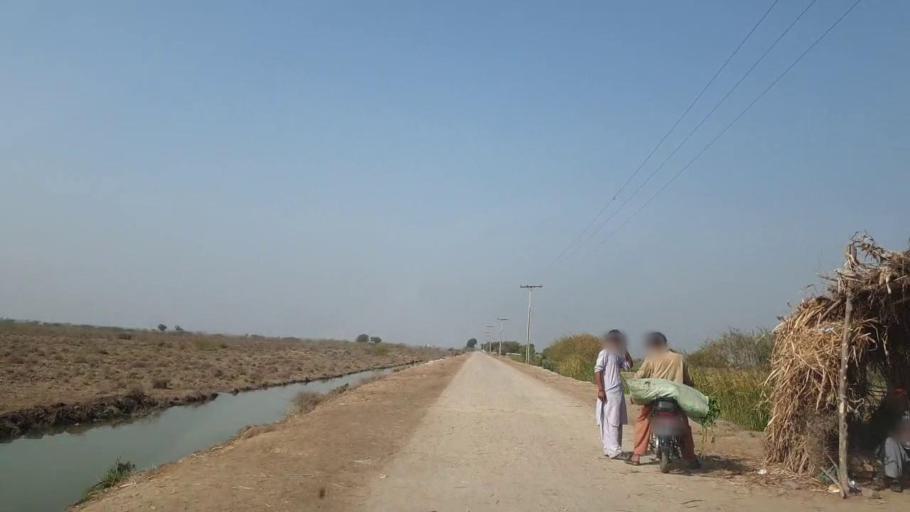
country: PK
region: Sindh
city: Mirpur Khas
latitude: 25.5828
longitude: 69.0369
